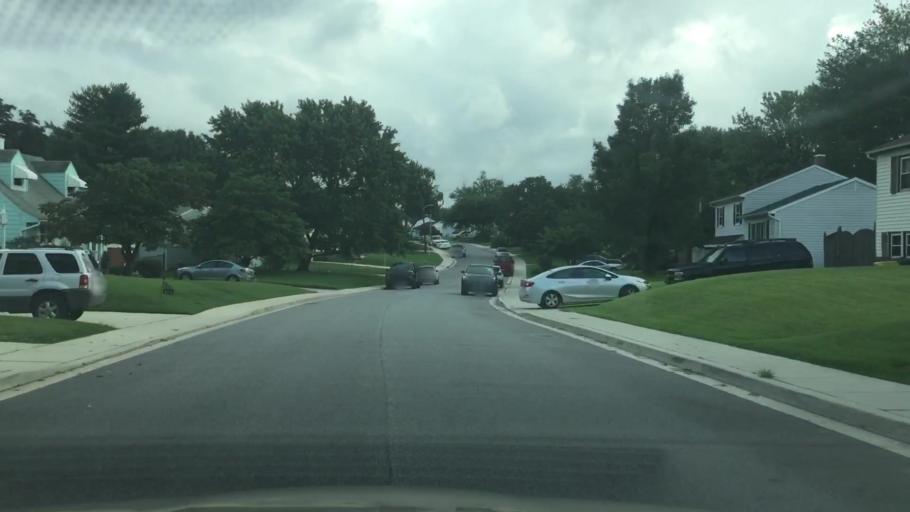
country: US
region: Maryland
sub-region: Anne Arundel County
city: South Gate
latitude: 39.1438
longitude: -76.6425
